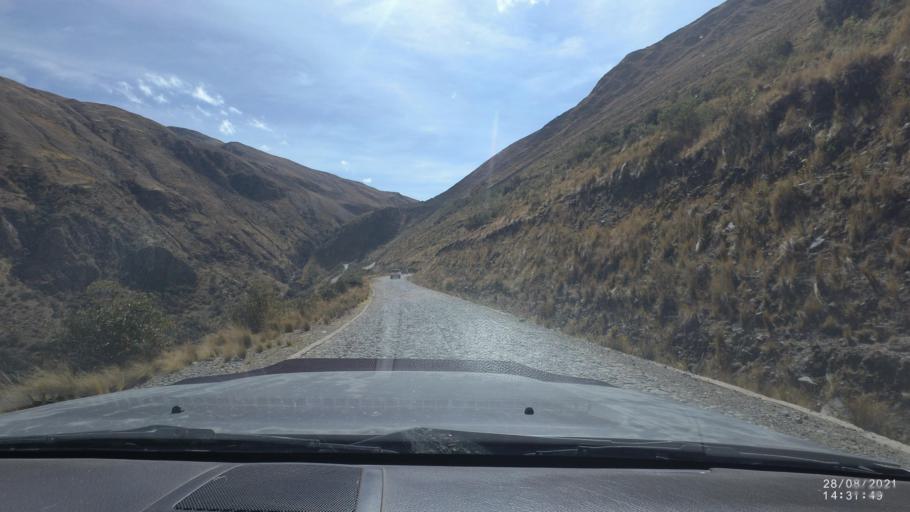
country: BO
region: Cochabamba
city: Sipe Sipe
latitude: -17.2690
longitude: -66.3361
